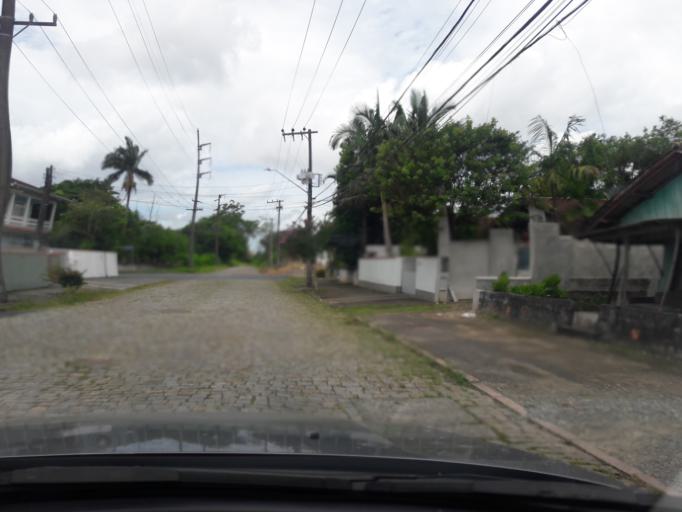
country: BR
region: Santa Catarina
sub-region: Joinville
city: Joinville
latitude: -26.3187
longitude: -48.8370
